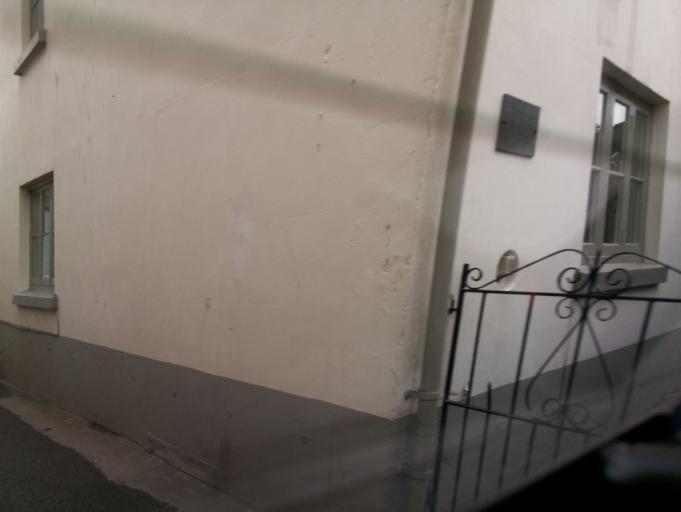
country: GB
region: England
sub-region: Devon
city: Salcombe
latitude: 50.2731
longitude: -3.6946
